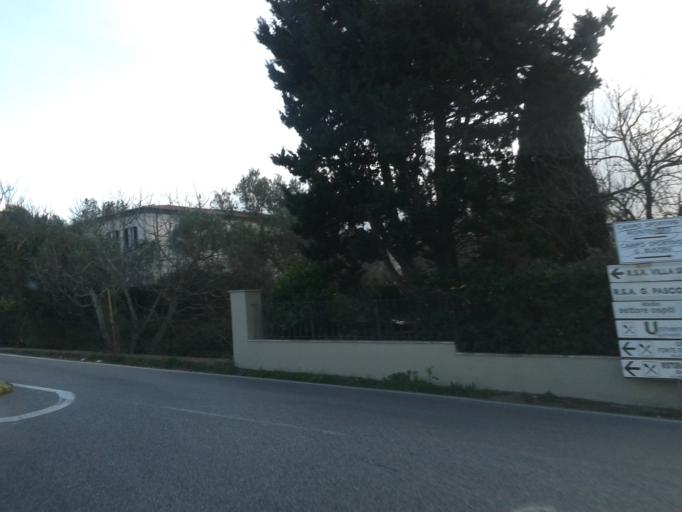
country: IT
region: Tuscany
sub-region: Provincia di Livorno
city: Livorno
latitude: 43.5095
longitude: 10.3337
